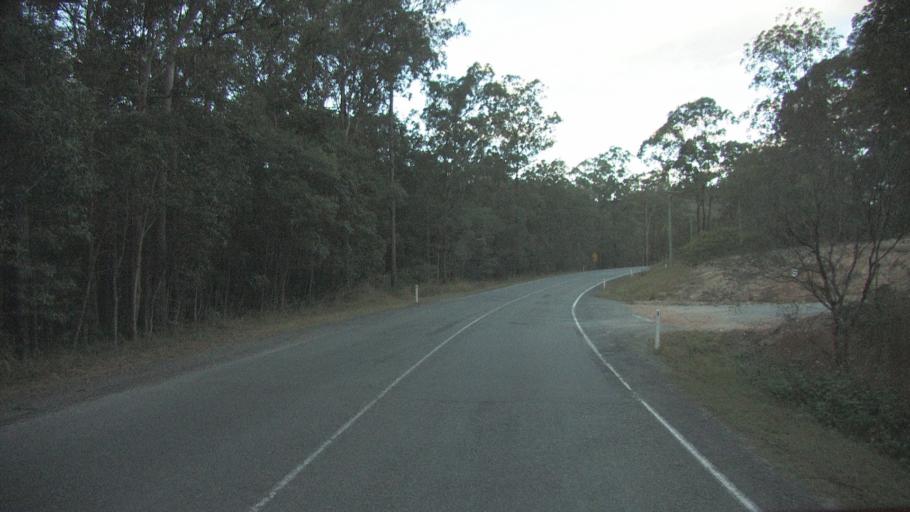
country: AU
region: Queensland
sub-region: Logan
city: Windaroo
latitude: -27.8074
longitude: 153.1507
